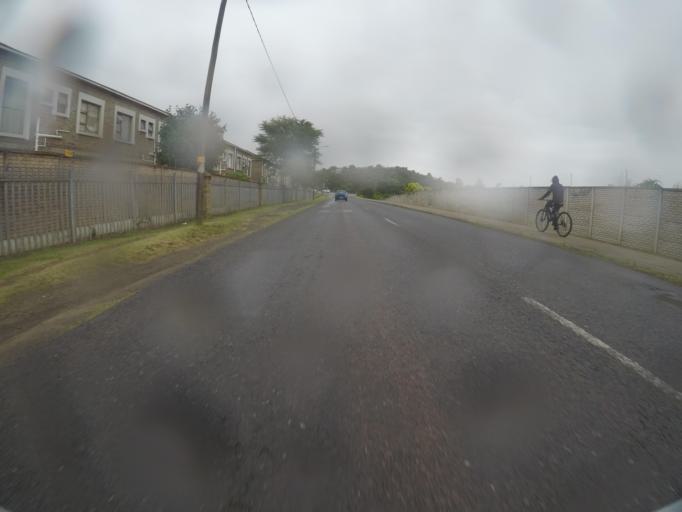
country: ZA
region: Eastern Cape
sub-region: Buffalo City Metropolitan Municipality
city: East London
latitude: -32.9610
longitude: 27.9163
